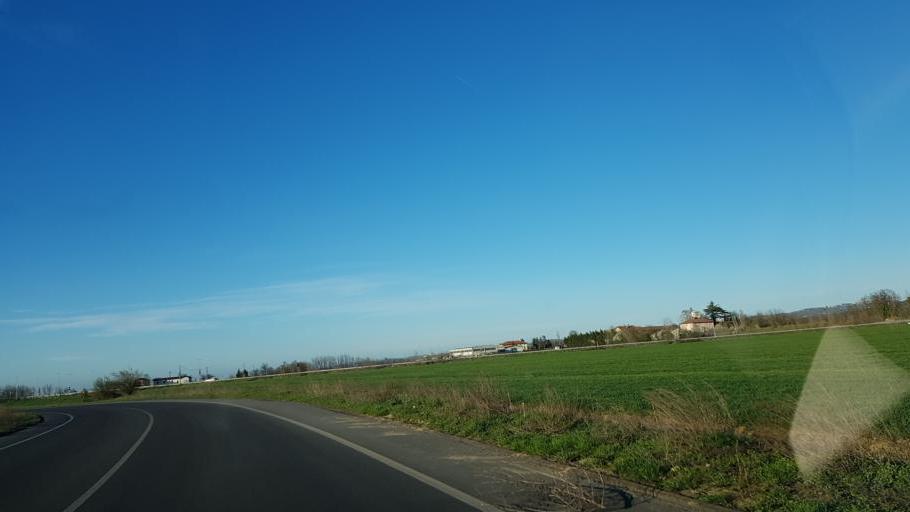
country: IT
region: Piedmont
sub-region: Provincia di Alessandria
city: Serravalle Scrivia
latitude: 44.7408
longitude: 8.8358
